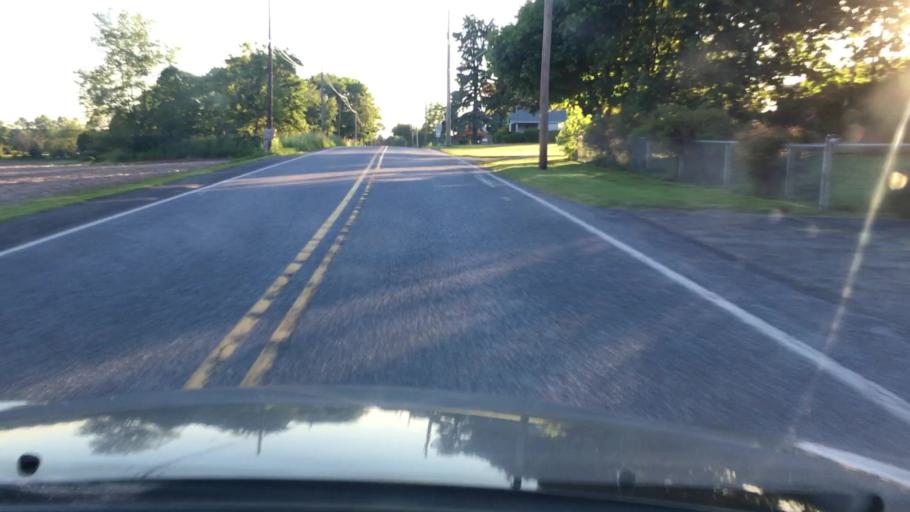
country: US
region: Pennsylvania
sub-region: Luzerne County
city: Harleigh
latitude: 41.0203
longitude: -75.9831
